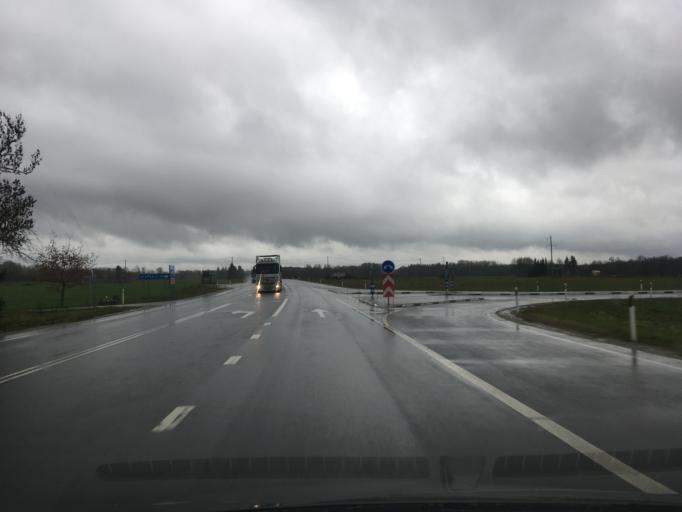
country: EE
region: Laeaene
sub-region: Lihula vald
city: Lihula
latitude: 58.7665
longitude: 23.9883
